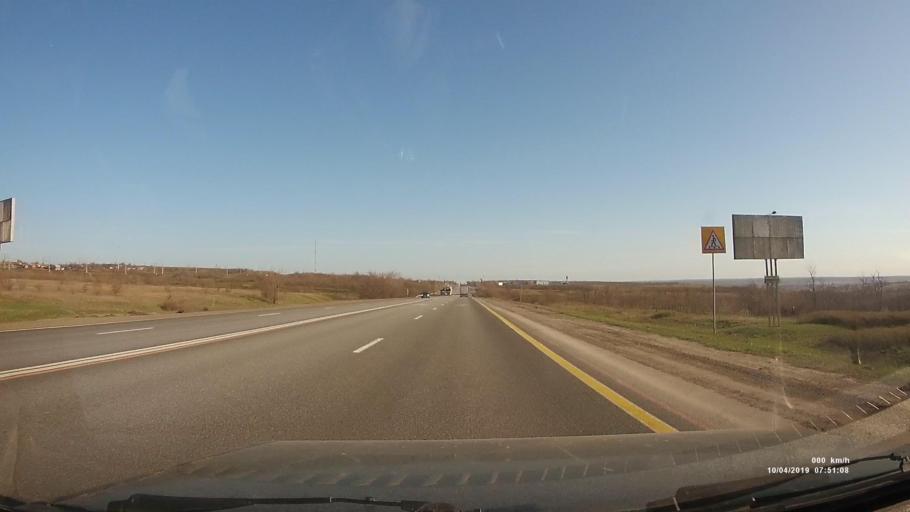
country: RU
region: Rostov
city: Kamensk-Shakhtinskiy
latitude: 48.2697
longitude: 40.2939
